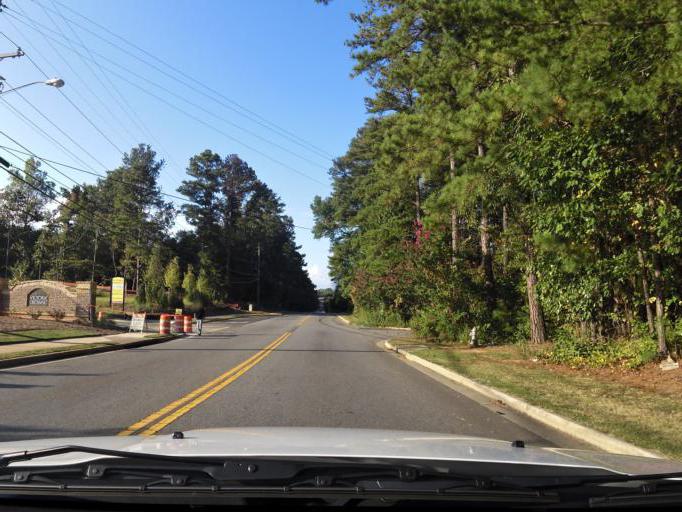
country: US
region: Georgia
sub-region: Cobb County
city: Kennesaw
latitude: 34.0400
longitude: -84.6162
